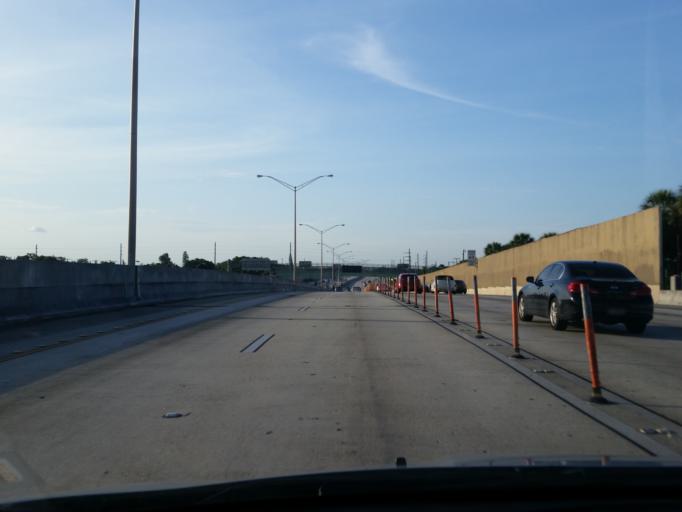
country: US
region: Florida
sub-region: Miami-Dade County
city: Allapattah
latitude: 25.8323
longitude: -80.2058
